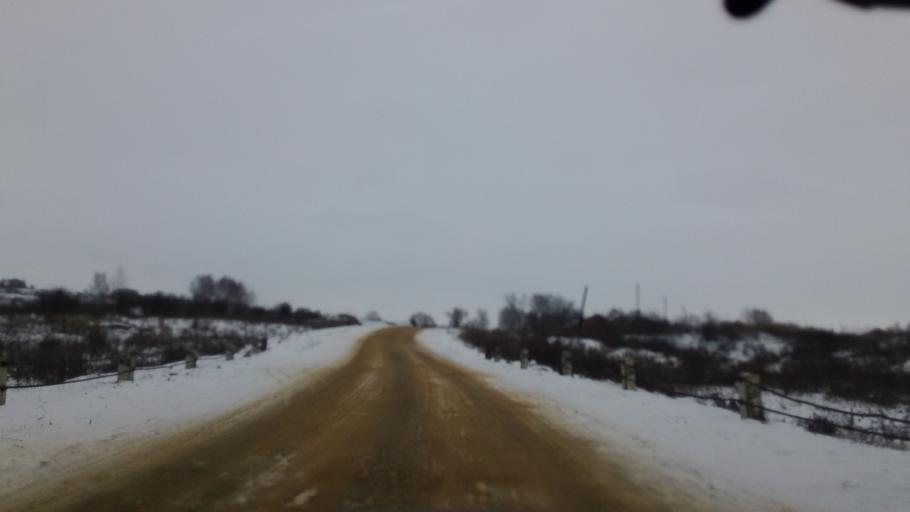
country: RU
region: Tula
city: Bogoroditsk
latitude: 53.7641
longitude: 37.9824
